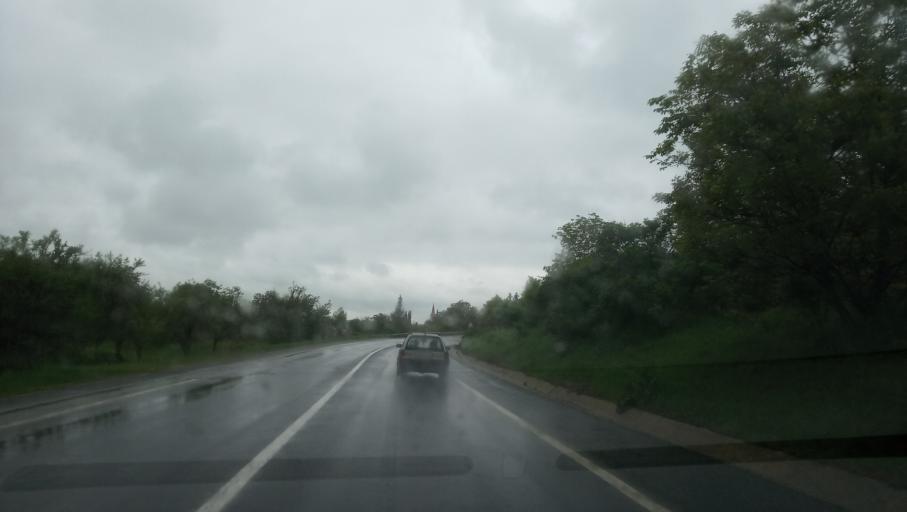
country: RO
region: Sibiu
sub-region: Comuna Apoldu de Jos
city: Apoldu de Jos
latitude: 45.8425
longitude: 23.8368
